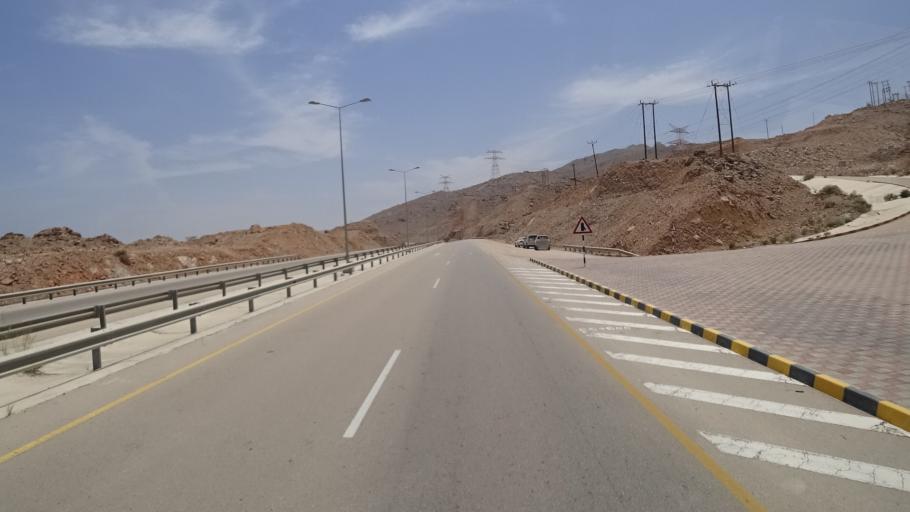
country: OM
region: Ash Sharqiyah
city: Sur
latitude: 22.6851
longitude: 59.3792
